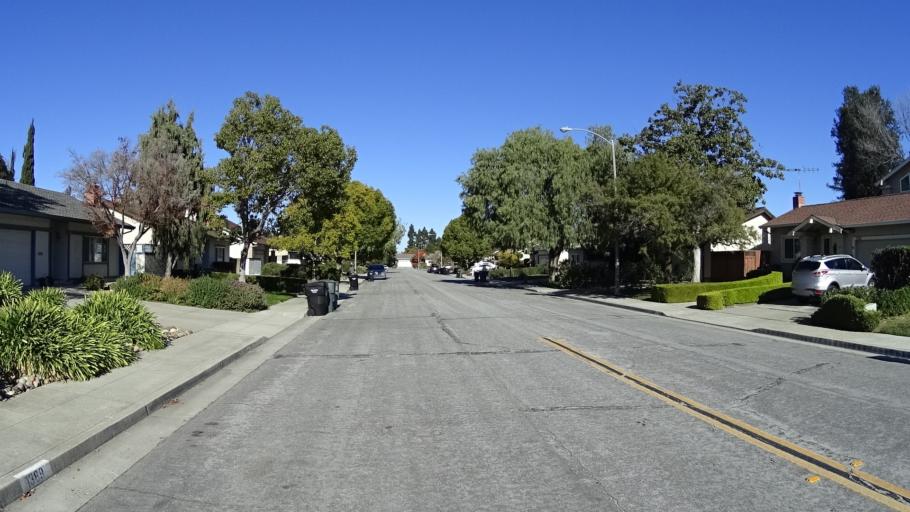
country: US
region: California
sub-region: Santa Clara County
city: Sunnyvale
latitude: 37.3492
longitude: -122.0035
